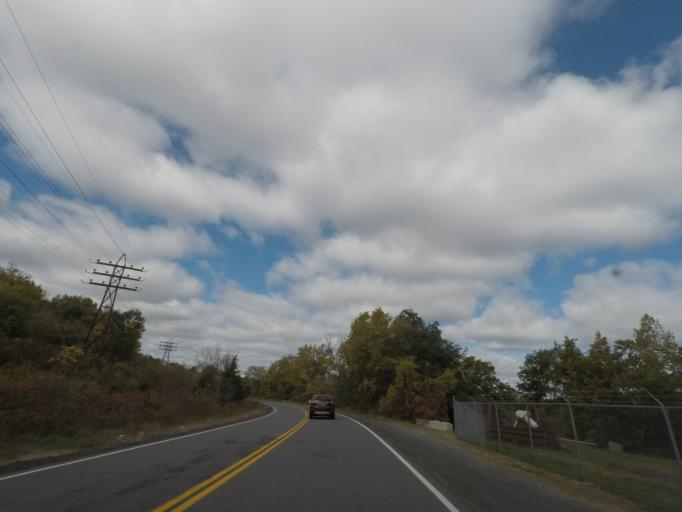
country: US
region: New York
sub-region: Albany County
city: Cohoes
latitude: 42.7973
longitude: -73.7167
